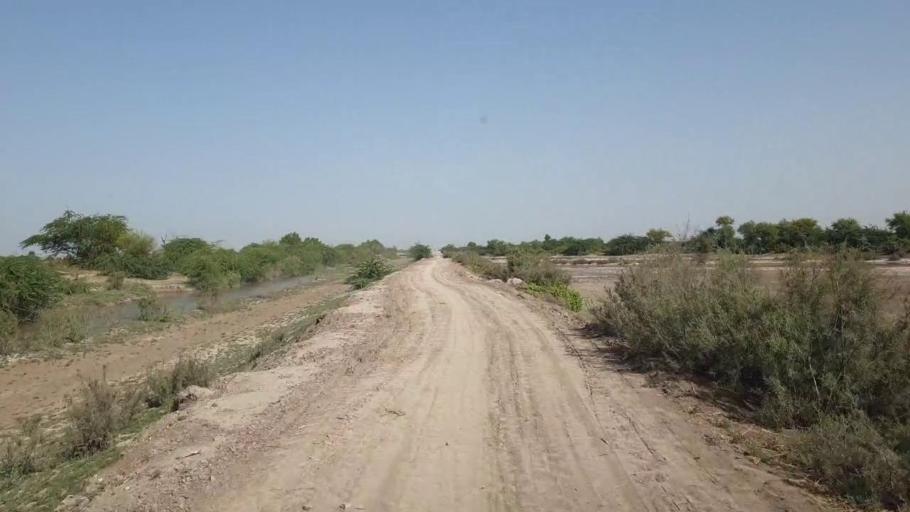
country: PK
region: Sindh
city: Tando Bago
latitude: 24.6658
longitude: 69.0676
